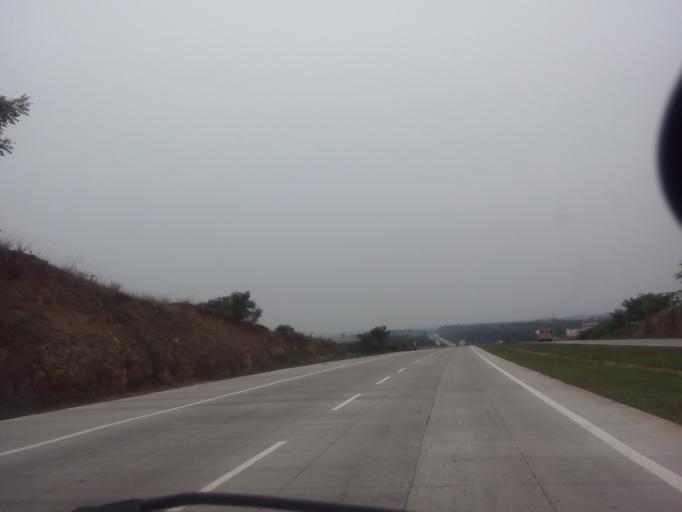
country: IN
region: Karnataka
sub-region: Bangalore Urban
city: Bangalore
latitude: 12.8861
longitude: 77.4868
